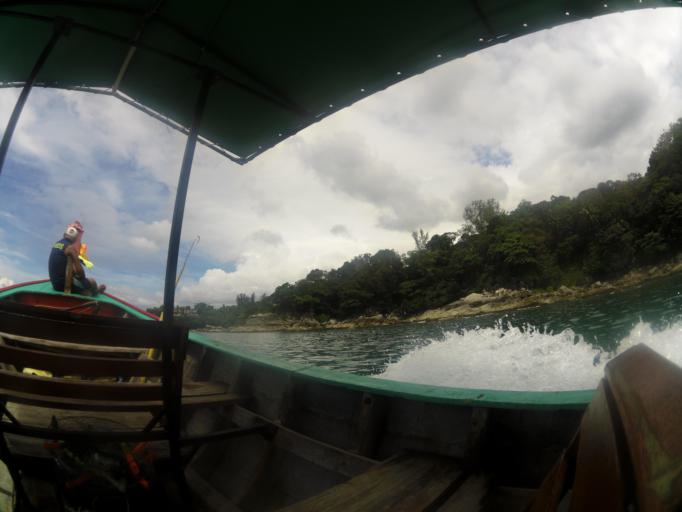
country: TH
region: Phuket
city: Patong
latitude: 7.9644
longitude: 98.2790
